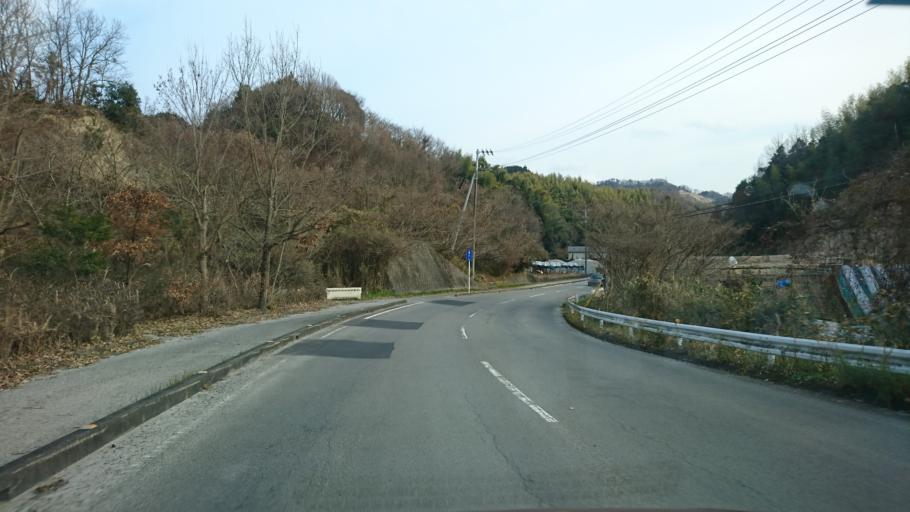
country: JP
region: Ehime
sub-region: Shikoku-chuo Shi
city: Matsuyama
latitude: 33.8966
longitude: 132.8061
